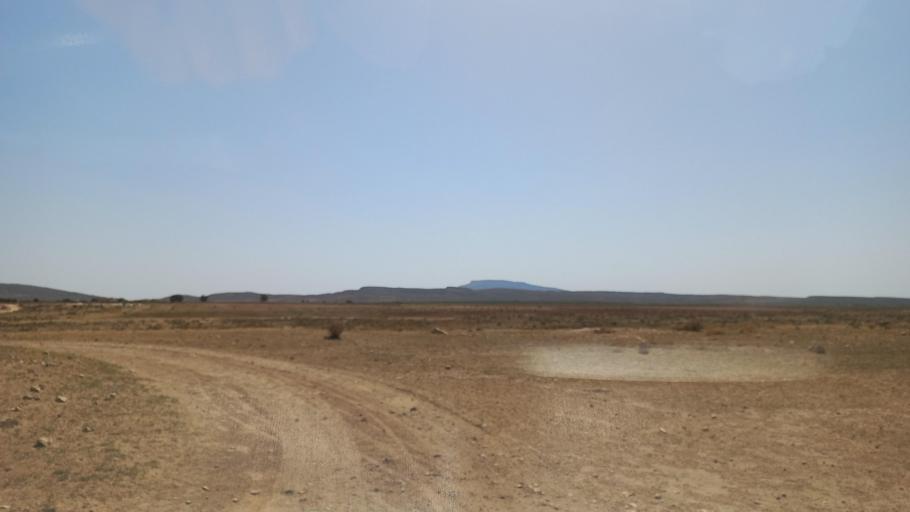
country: TN
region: Al Qasrayn
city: Kasserine
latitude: 35.2242
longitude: 9.0353
